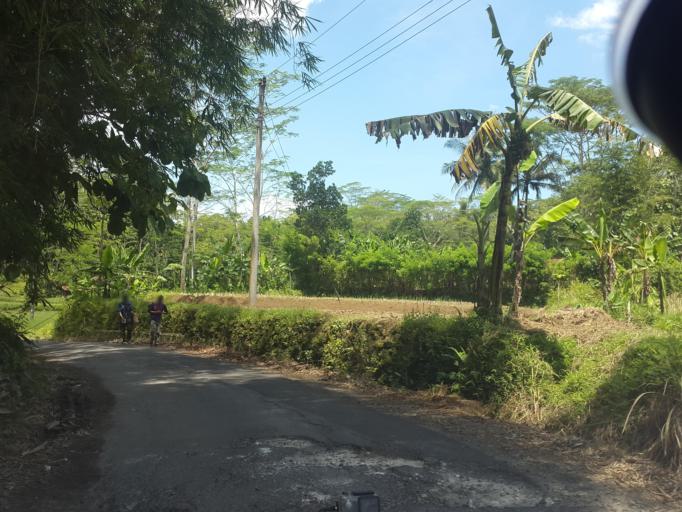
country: ID
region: Central Java
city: Sangkalputung
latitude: -7.4150
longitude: 109.0469
